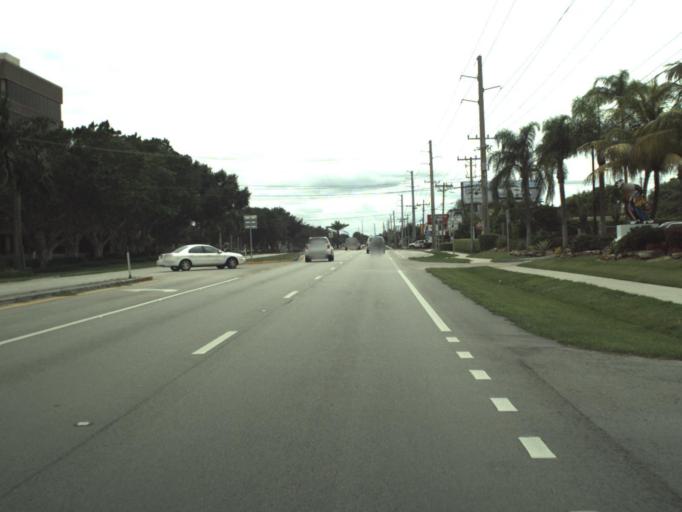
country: US
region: Florida
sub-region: Palm Beach County
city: Juno Beach
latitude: 26.8506
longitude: -80.0592
